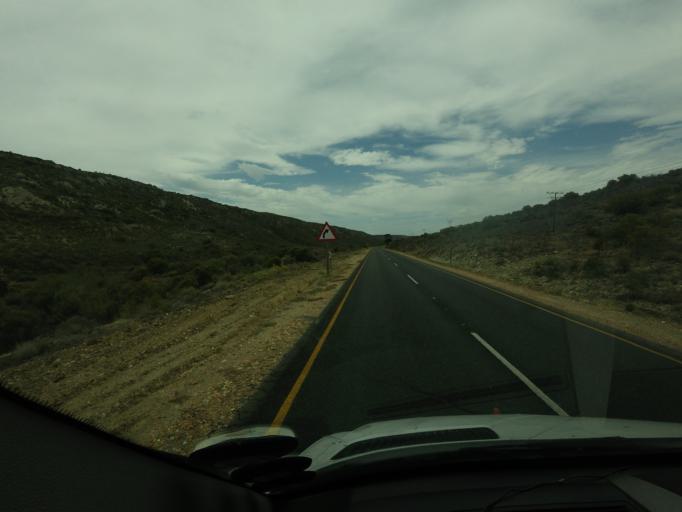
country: ZA
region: Western Cape
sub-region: Overberg District Municipality
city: Swellendam
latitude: -33.8582
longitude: 20.7906
